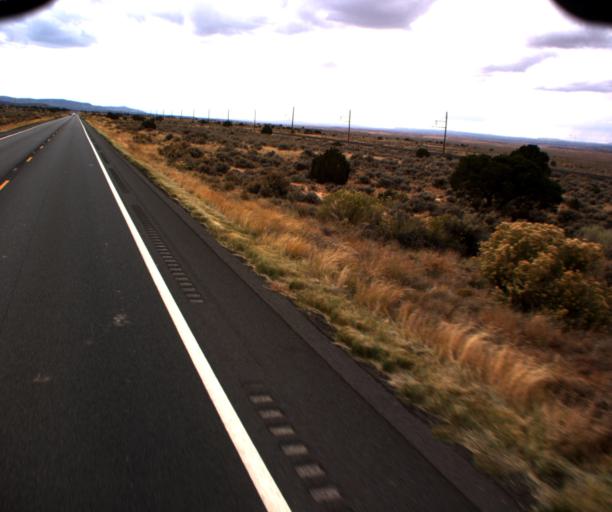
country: US
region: Arizona
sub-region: Navajo County
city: Kayenta
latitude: 36.5095
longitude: -110.6045
